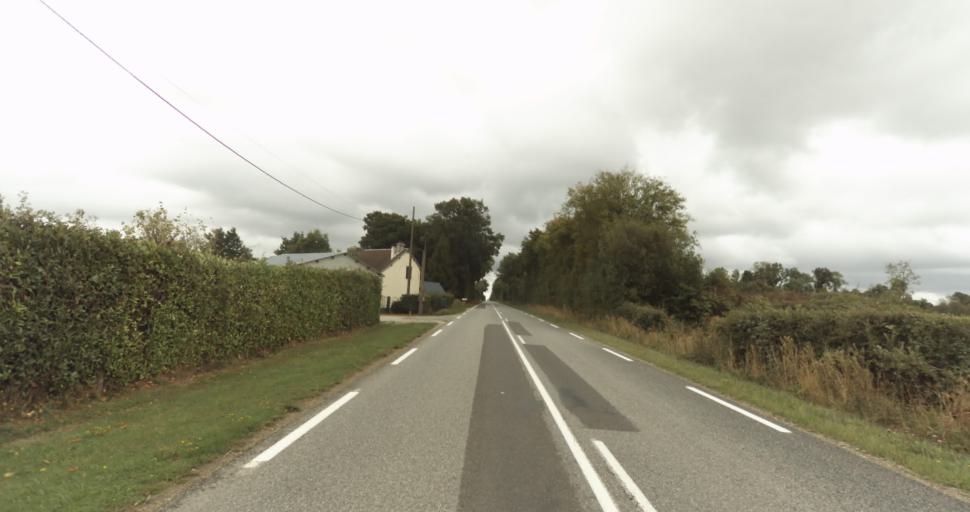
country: FR
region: Lower Normandy
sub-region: Departement de l'Orne
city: Sainte-Gauburge-Sainte-Colombe
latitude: 48.6980
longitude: 0.4416
